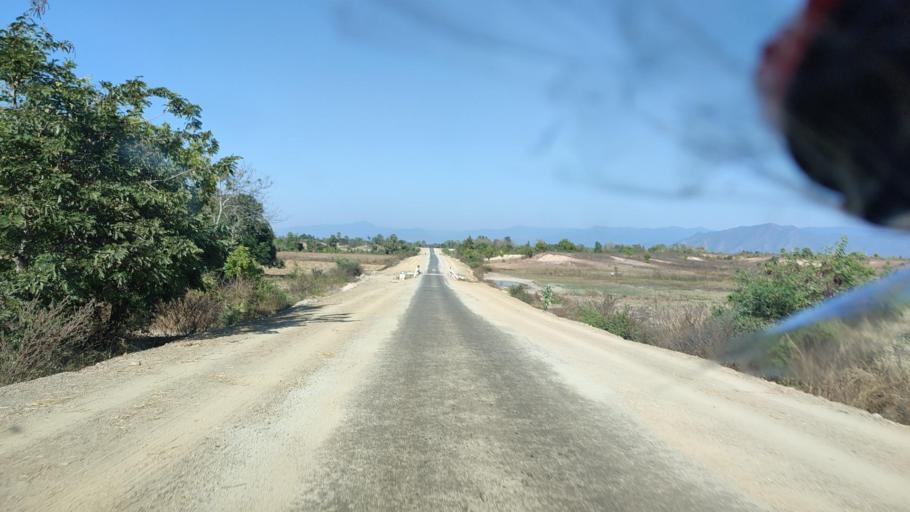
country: MM
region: Mandalay
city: Yamethin
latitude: 20.1122
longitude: 96.2694
